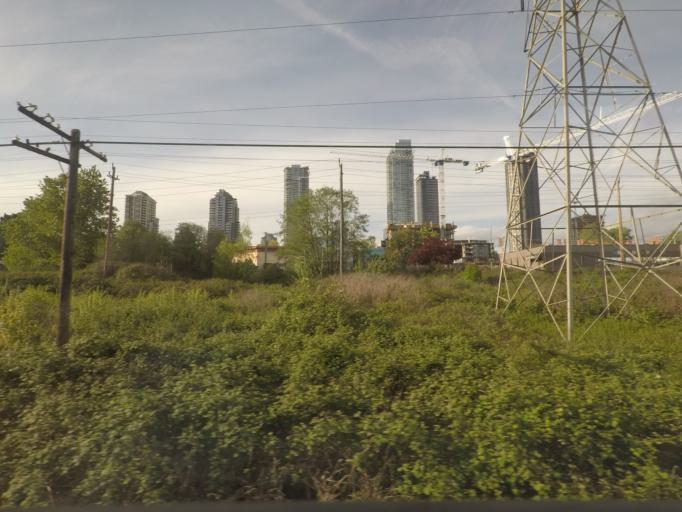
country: CA
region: British Columbia
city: Burnaby
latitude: 49.2621
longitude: -123.0050
